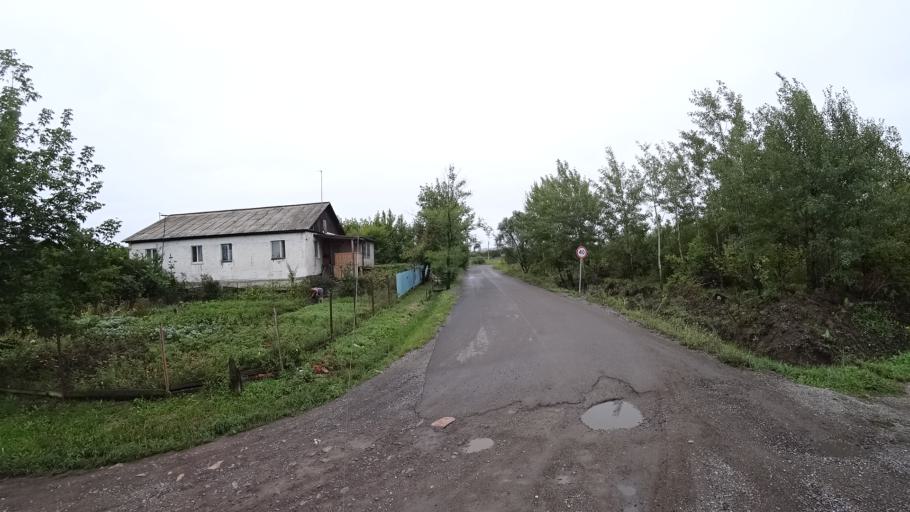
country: RU
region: Primorskiy
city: Monastyrishche
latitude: 44.2105
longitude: 132.4366
